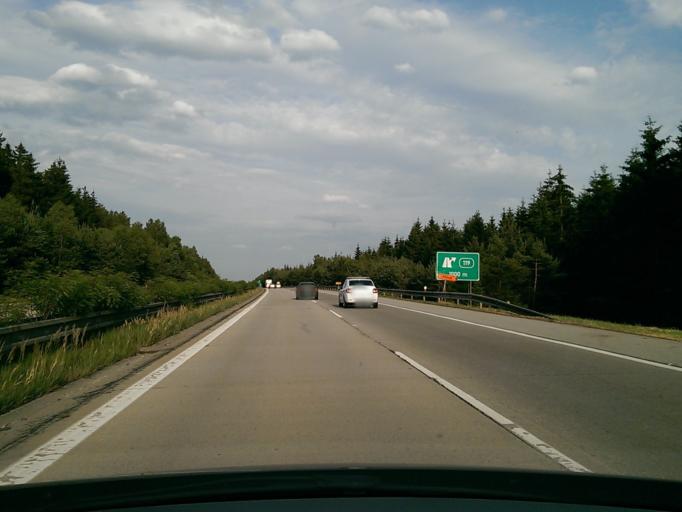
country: CZ
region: Vysocina
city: Velky Beranov
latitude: 49.4253
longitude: 15.6701
